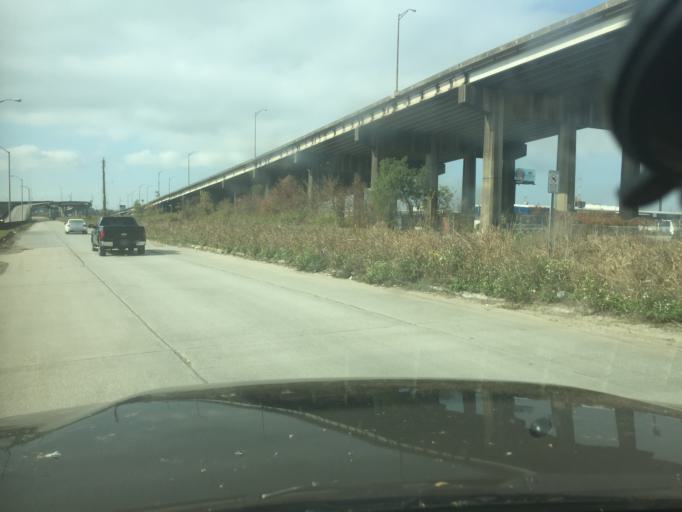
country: US
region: Louisiana
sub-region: Saint Bernard Parish
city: Arabi
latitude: 30.0033
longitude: -90.0307
